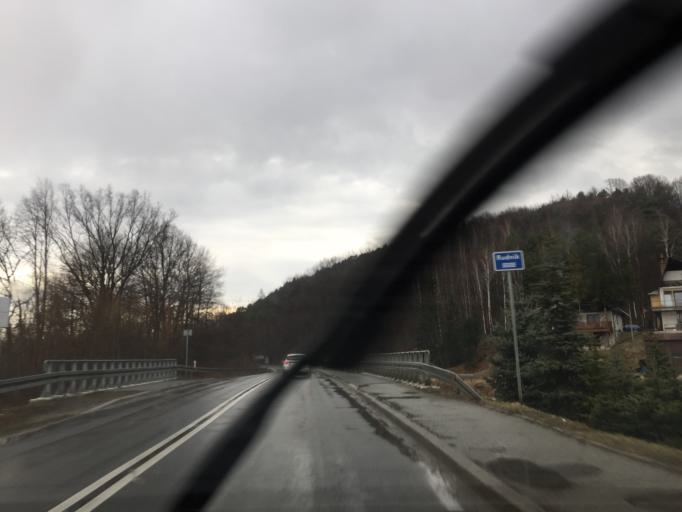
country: PL
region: Lesser Poland Voivodeship
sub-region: Powiat myslenicki
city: Sulkowice
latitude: 49.8626
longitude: 19.7962
